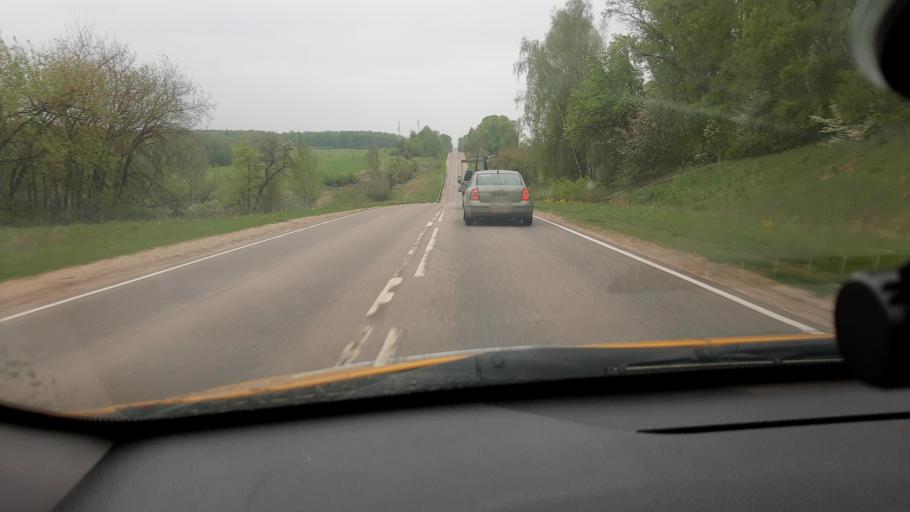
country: RU
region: Tula
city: Zaokskiy
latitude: 54.7810
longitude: 37.4345
